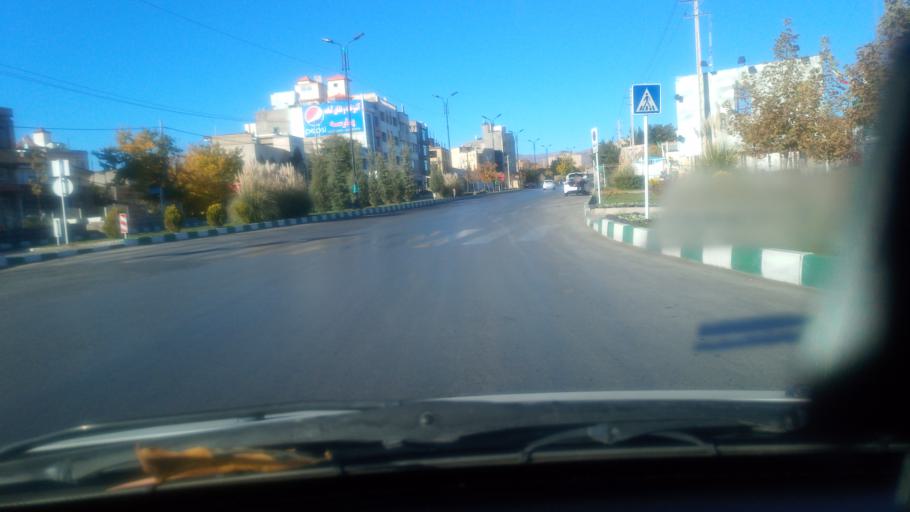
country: IR
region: Razavi Khorasan
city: Torqabeh
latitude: 36.3141
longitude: 59.3761
